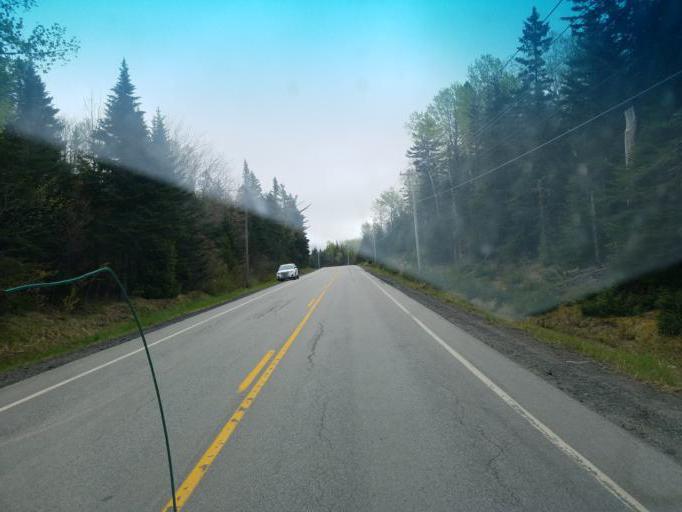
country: US
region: Maine
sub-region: Washington County
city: Eastport
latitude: 44.8042
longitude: -67.1044
